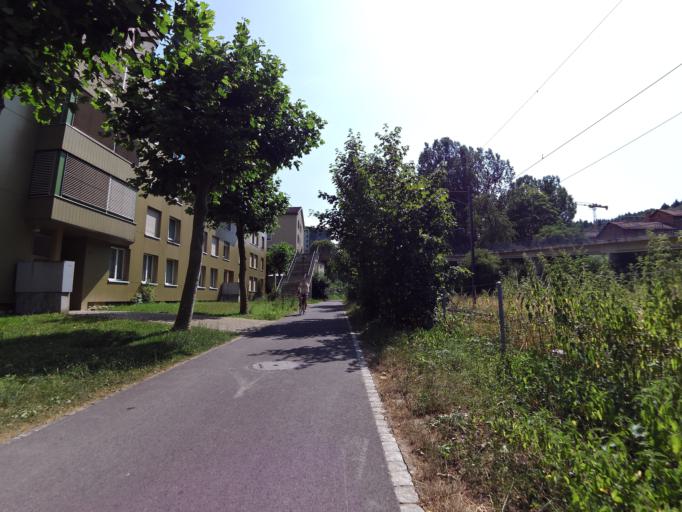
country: CH
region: Aargau
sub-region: Bezirk Baden
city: Baden
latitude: 47.4659
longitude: 8.2898
